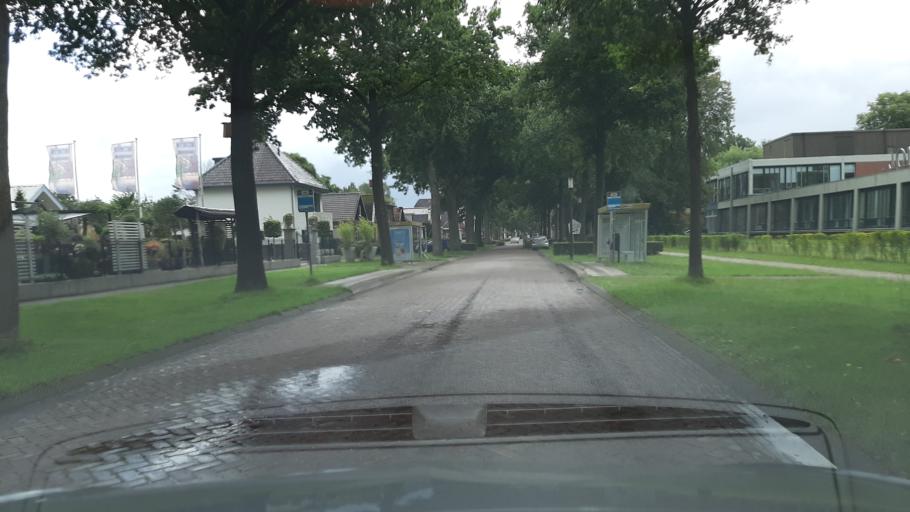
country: NL
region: Friesland
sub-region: Gemeente Heerenveen
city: Oudeschoot
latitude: 52.9383
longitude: 5.9501
